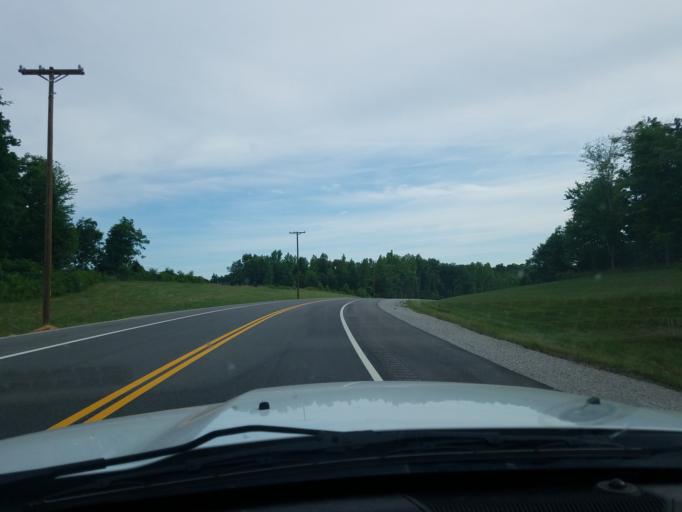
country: US
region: Tennessee
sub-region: Putnam County
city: Cookeville
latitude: 36.1549
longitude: -85.5649
